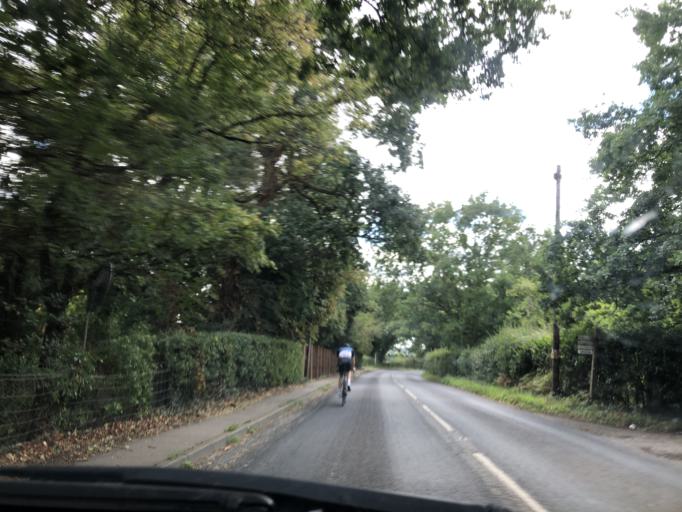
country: GB
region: England
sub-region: Kent
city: Edenbridge
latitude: 51.2272
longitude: 0.0605
